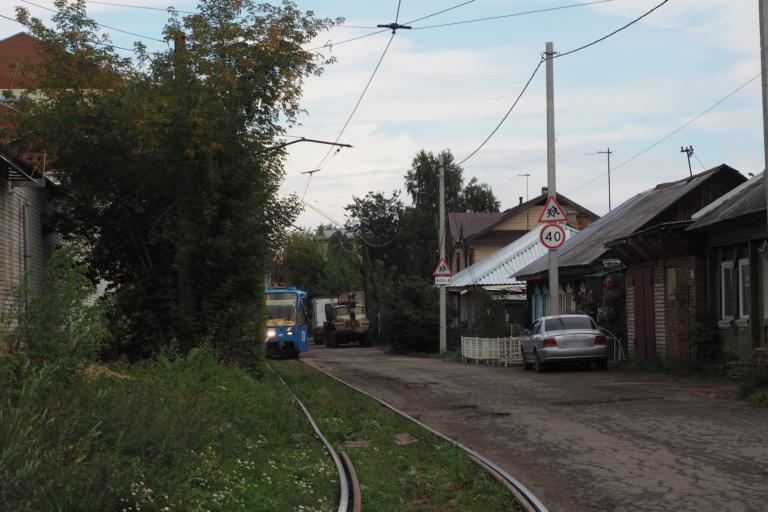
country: RU
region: Tomsk
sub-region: Tomskiy Rayon
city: Tomsk
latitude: 56.4785
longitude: 85.0031
